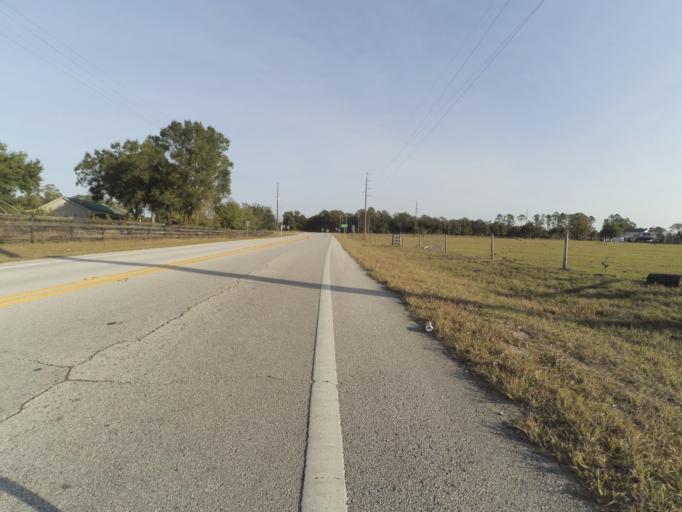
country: US
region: Florida
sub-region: Lake County
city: Umatilla
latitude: 28.9590
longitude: -81.6278
